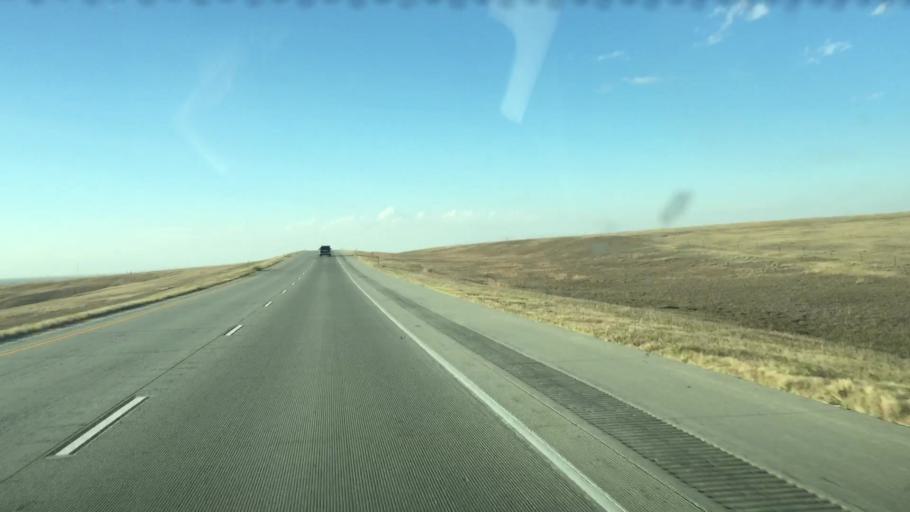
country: US
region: Colorado
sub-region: Lincoln County
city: Limon
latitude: 39.3985
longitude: -103.8921
